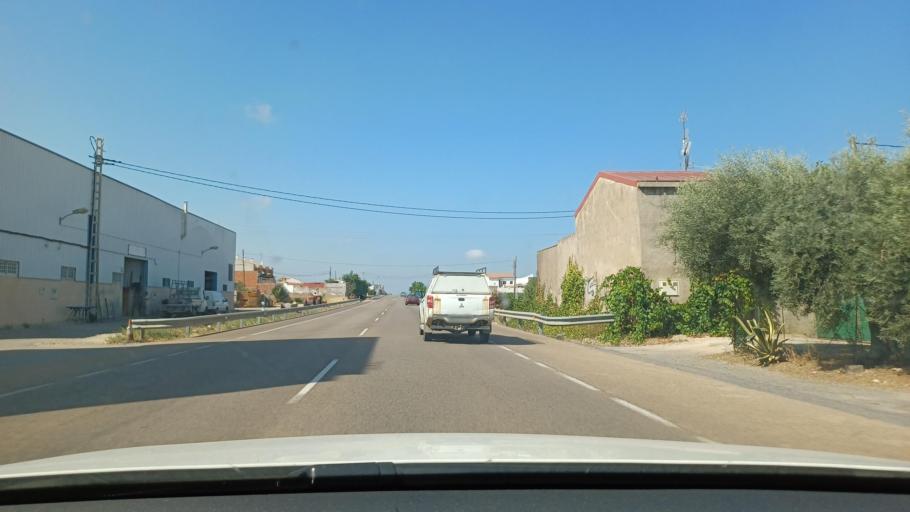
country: ES
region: Valencia
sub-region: Provincia de Castello
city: Orpesa/Oropesa del Mar
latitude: 40.1525
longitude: 0.1582
